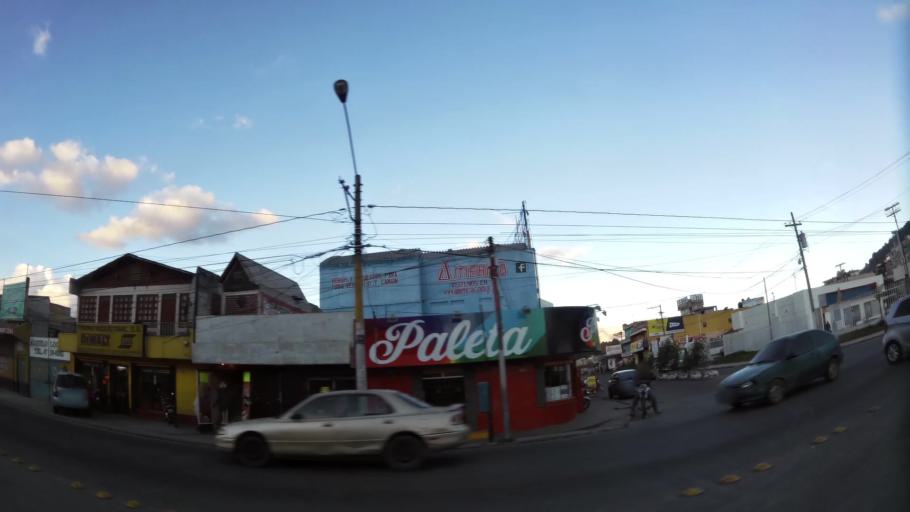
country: GT
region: Quetzaltenango
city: Quetzaltenango
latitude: 14.8393
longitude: -91.5081
